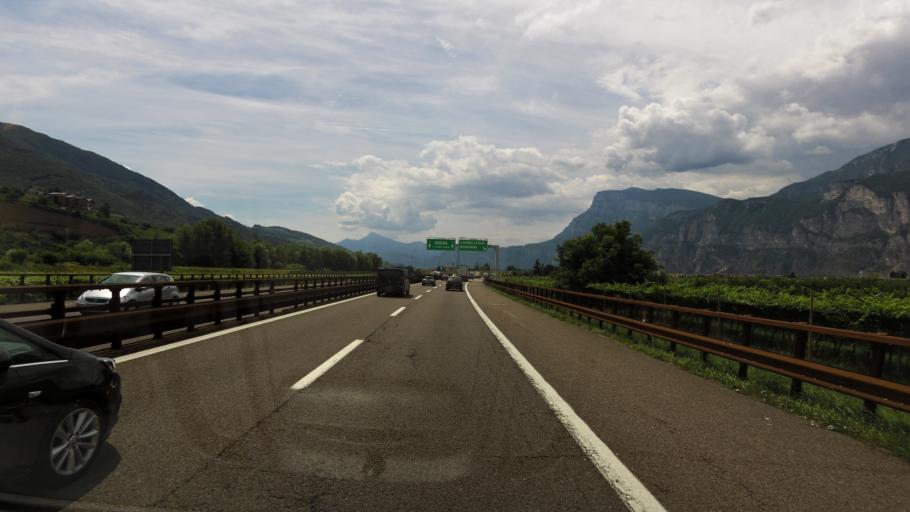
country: IT
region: Trentino-Alto Adige
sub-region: Provincia di Trento
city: San Michele All'Adige
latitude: 46.2040
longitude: 11.1366
